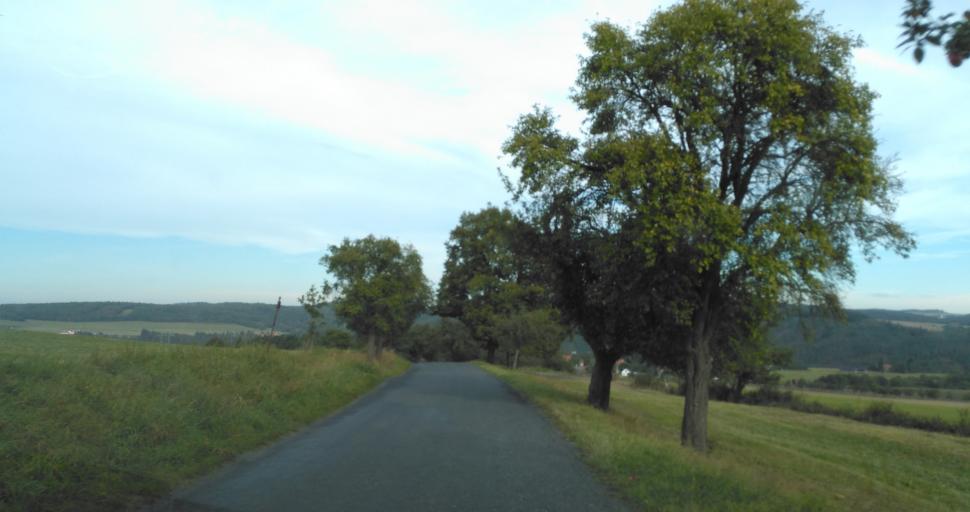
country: CZ
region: Plzensky
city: Zbiroh
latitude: 49.9581
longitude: 13.7731
